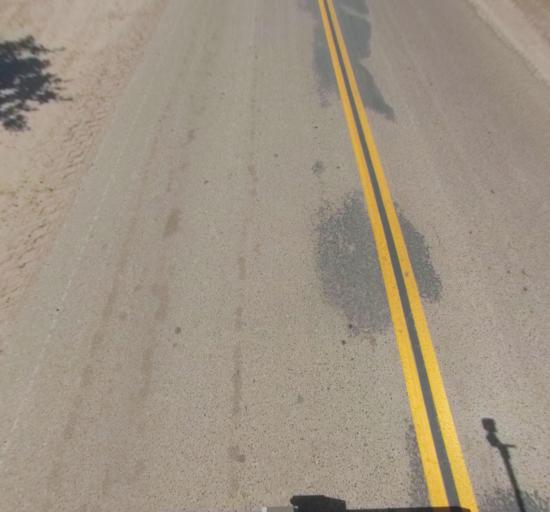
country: US
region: California
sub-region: Fresno County
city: Mendota
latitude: 36.8083
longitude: -120.2591
